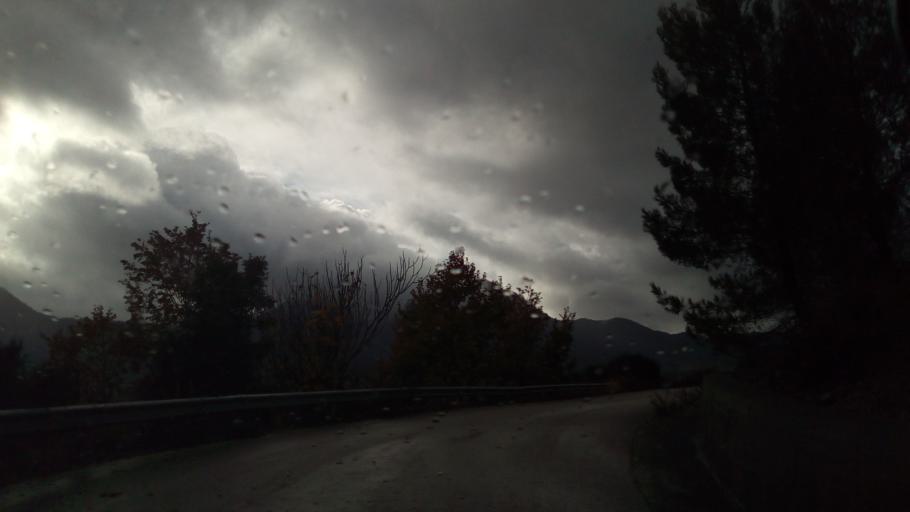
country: GR
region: West Greece
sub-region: Nomos Aitolias kai Akarnanias
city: Thermo
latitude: 38.6746
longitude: 21.8550
